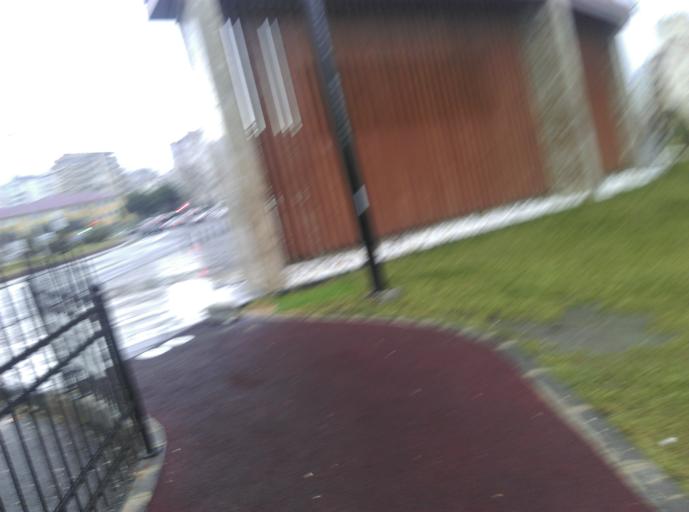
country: TR
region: Kahramanmaras
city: Kahramanmaras
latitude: 37.5833
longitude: 36.8898
